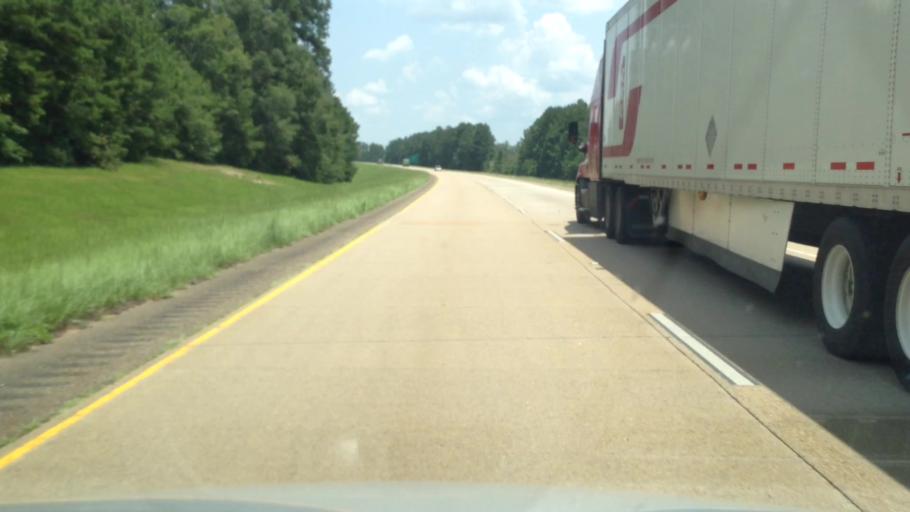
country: US
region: Louisiana
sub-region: Rapides Parish
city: Lecompte
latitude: 31.0350
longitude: -92.4128
